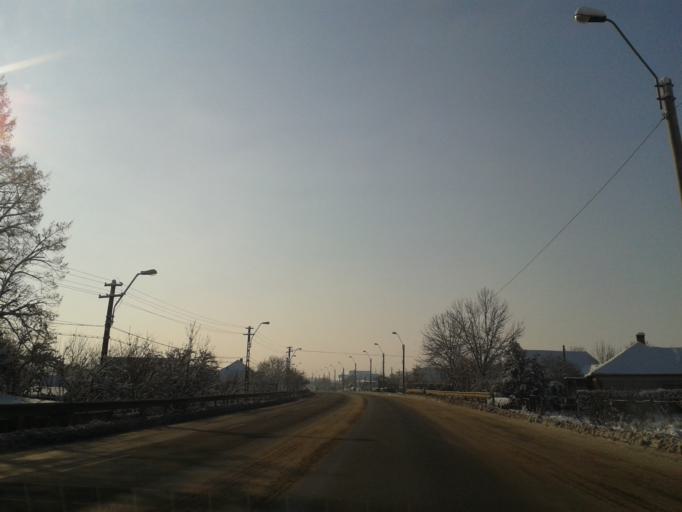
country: RO
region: Hunedoara
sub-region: Municipiul Hunedoara
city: Pestisu Mare
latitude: 45.8031
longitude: 22.9232
